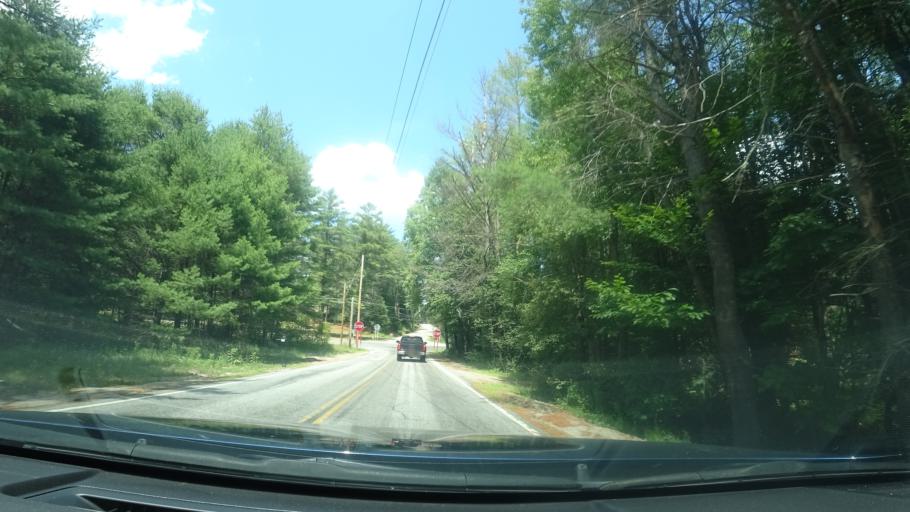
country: US
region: New York
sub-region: Warren County
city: Warrensburg
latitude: 43.6627
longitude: -73.8359
